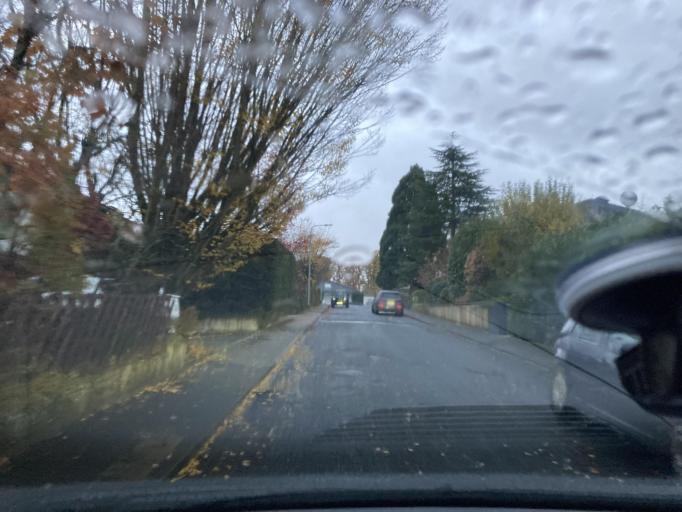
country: DE
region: Hesse
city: Kelkheim (Taunus)
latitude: 50.1351
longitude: 8.4378
